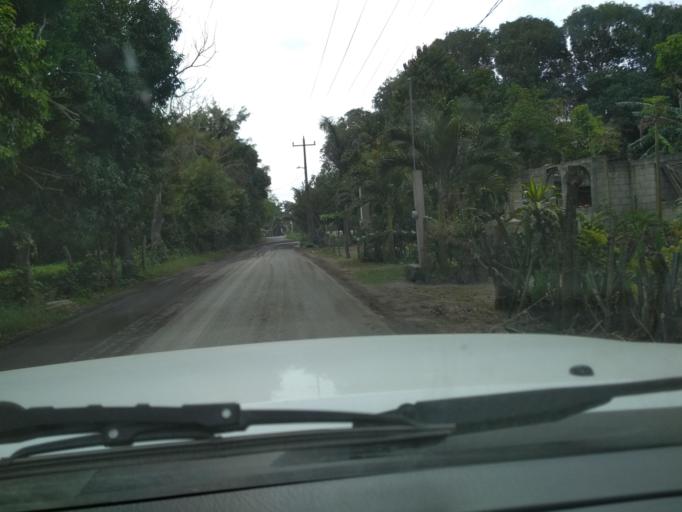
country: MX
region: Veracruz
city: El Tejar
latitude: 19.0783
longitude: -96.1720
